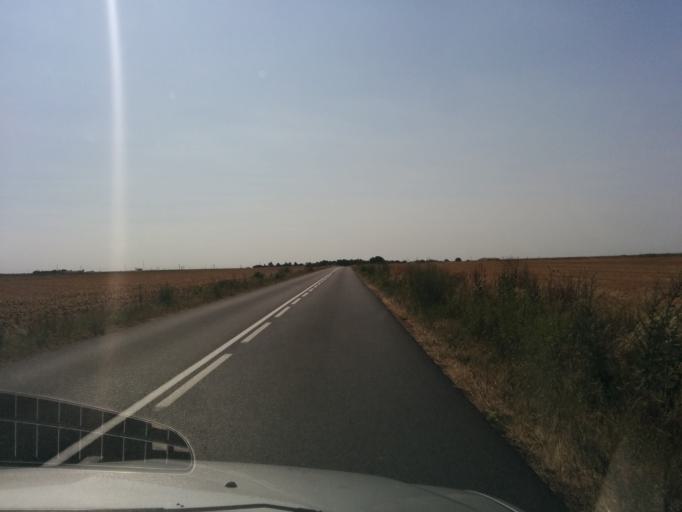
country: FR
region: Poitou-Charentes
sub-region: Departement de la Vienne
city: Moncontour
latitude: 46.8082
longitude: -0.0168
